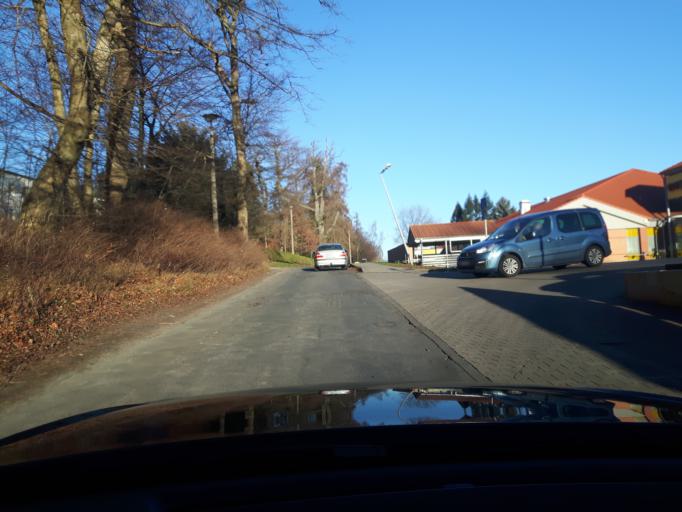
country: DE
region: Mecklenburg-Vorpommern
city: Putbus
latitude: 54.3519
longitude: 13.4641
